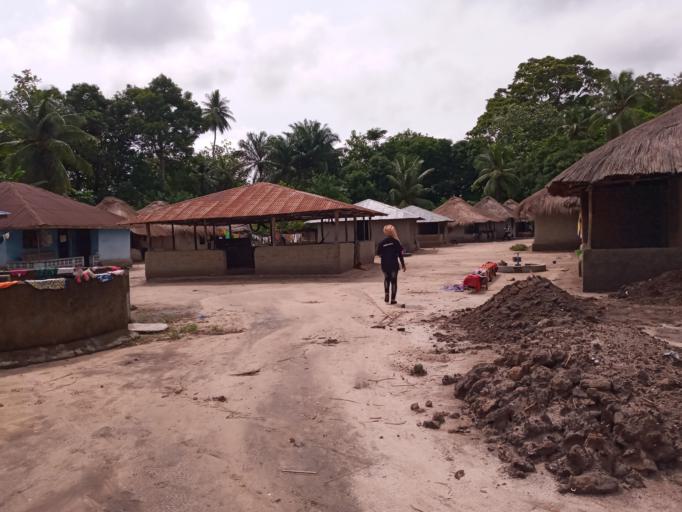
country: SL
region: Southern Province
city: Bonthe
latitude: 7.5242
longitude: -12.5753
